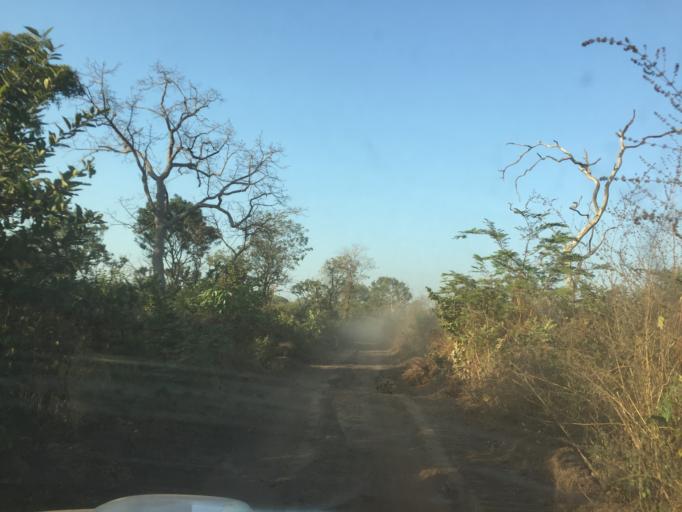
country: GW
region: Oio
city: Farim
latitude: 12.5295
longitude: -15.2761
